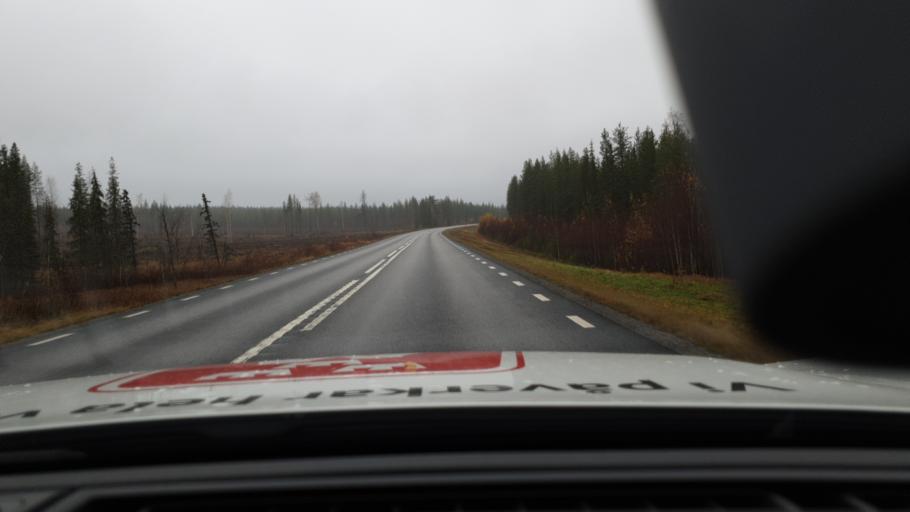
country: SE
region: Norrbotten
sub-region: Overkalix Kommun
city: OEverkalix
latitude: 66.6085
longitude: 22.2476
